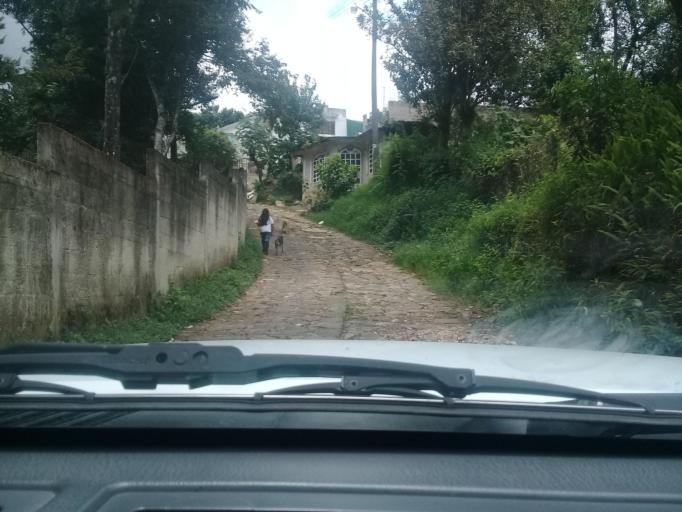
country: MX
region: Veracruz
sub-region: Tlalnelhuayocan
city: Otilpan
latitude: 19.5475
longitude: -96.9741
